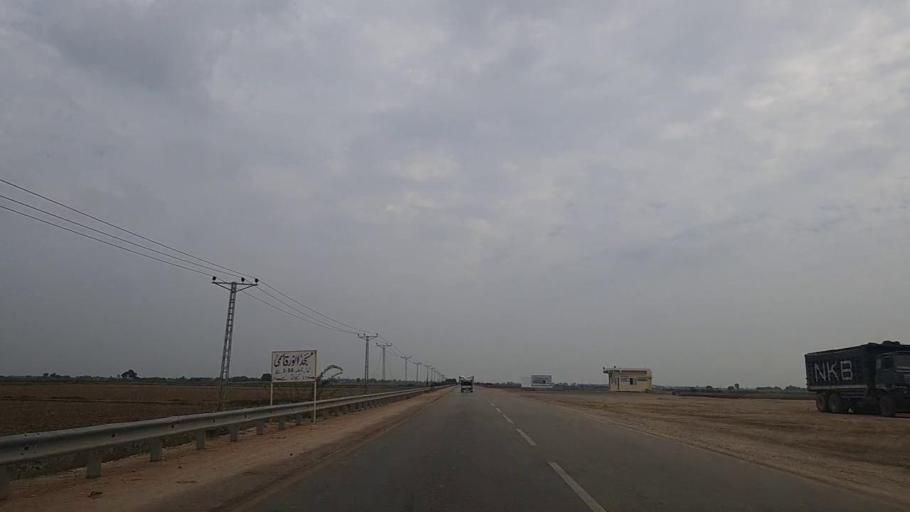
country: PK
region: Sindh
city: Thatta
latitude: 24.6157
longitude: 68.0612
